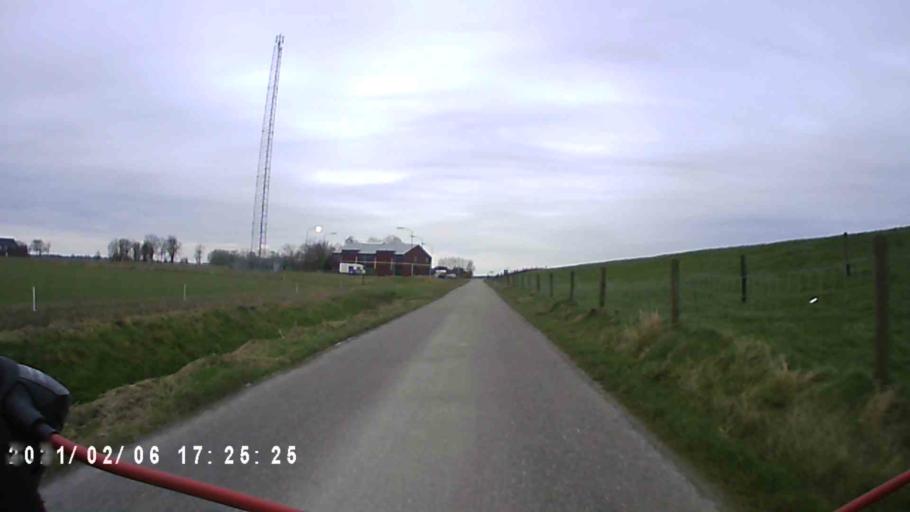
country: NL
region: Groningen
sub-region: Gemeente Appingedam
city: Appingedam
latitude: 53.4365
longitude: 6.7957
